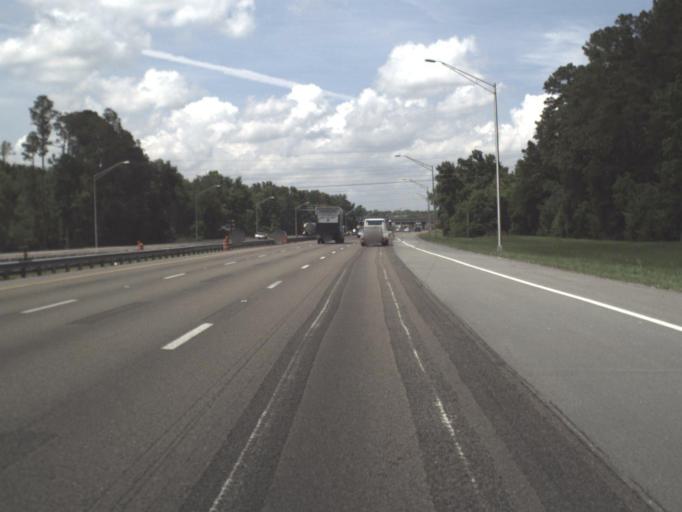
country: US
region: Florida
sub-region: Clay County
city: Bellair-Meadowbrook Terrace
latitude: 30.2204
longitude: -81.7618
